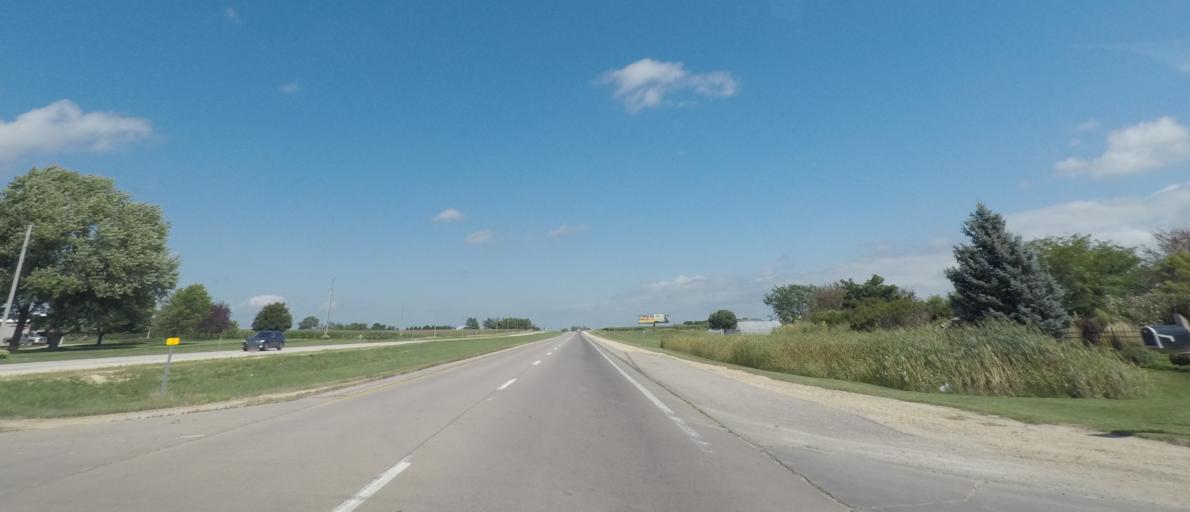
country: US
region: Iowa
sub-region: Linn County
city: Marion
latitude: 42.0375
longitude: -91.5307
